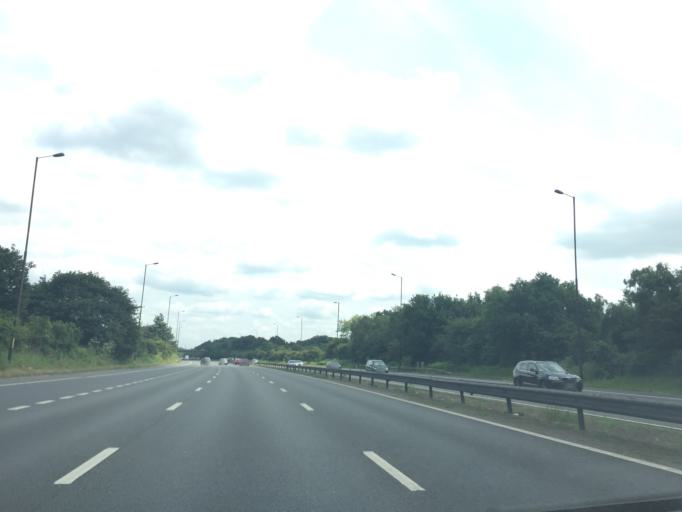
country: GB
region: England
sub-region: Kent
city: Dartford
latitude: 51.4341
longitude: 0.1846
